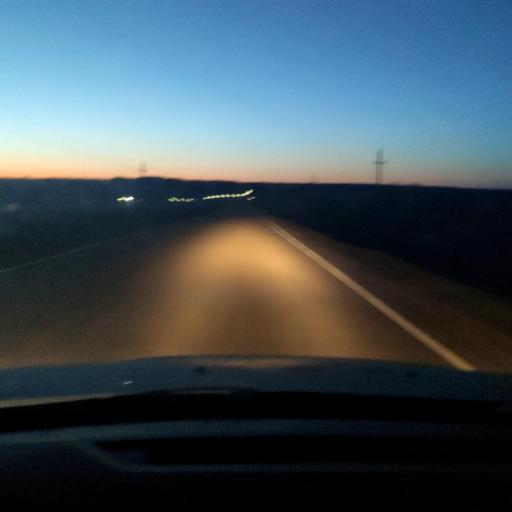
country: RU
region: Bashkortostan
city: Ulukulevo
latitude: 54.5580
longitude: 56.3438
